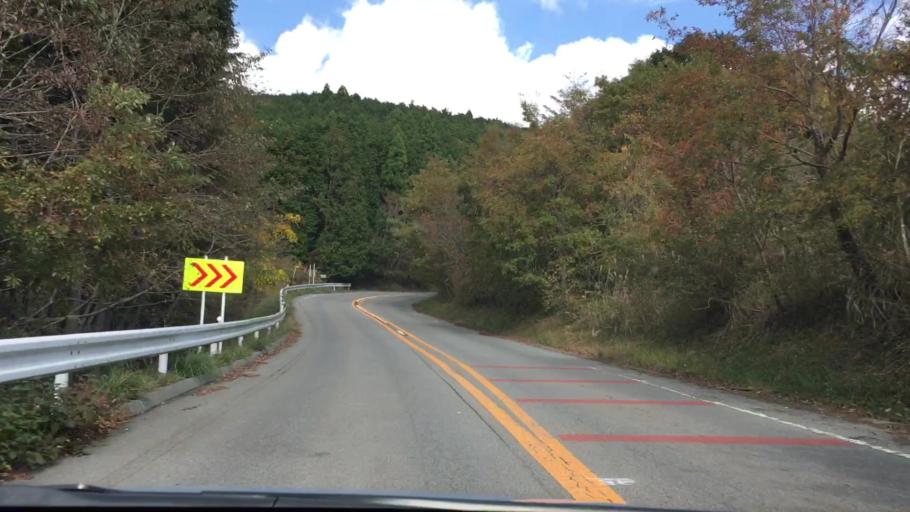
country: JP
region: Shizuoka
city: Gotemba
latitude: 35.3852
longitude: 138.9441
